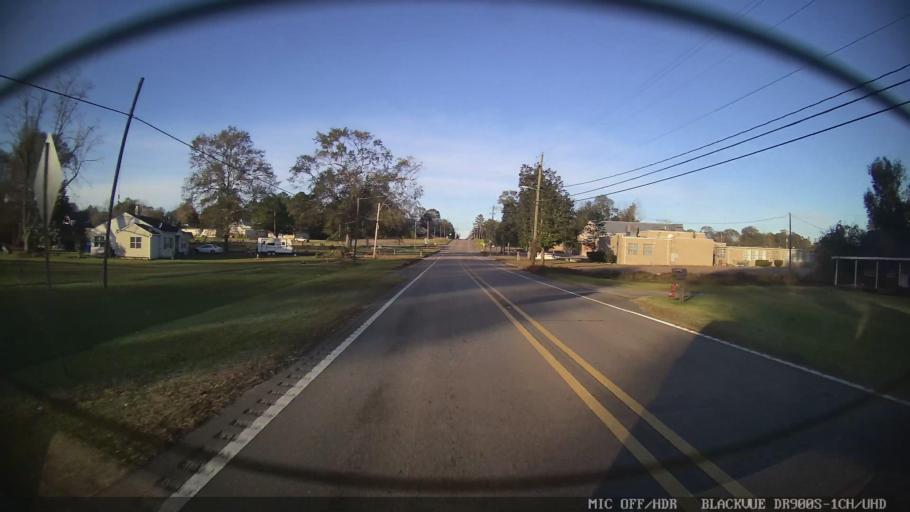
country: US
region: Mississippi
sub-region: Lamar County
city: Lumberton
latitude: 30.9970
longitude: -89.4544
